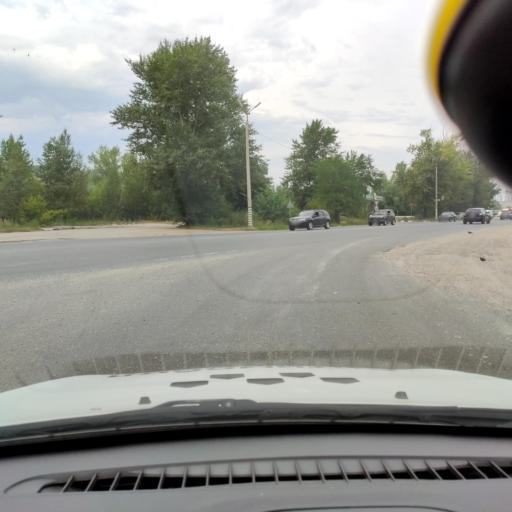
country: RU
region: Samara
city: Zhigulevsk
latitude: 53.4150
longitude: 49.4824
